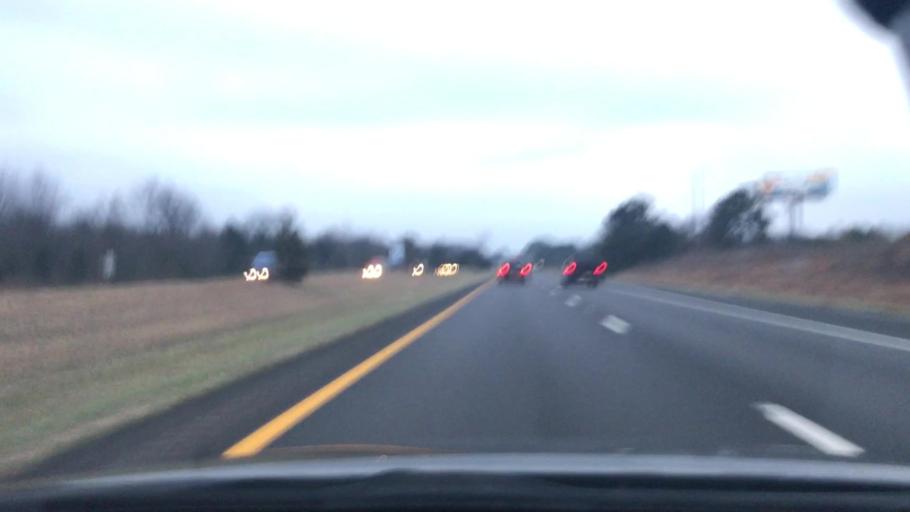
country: US
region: Tennessee
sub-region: Sumner County
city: White House
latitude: 36.4624
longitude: -86.6874
